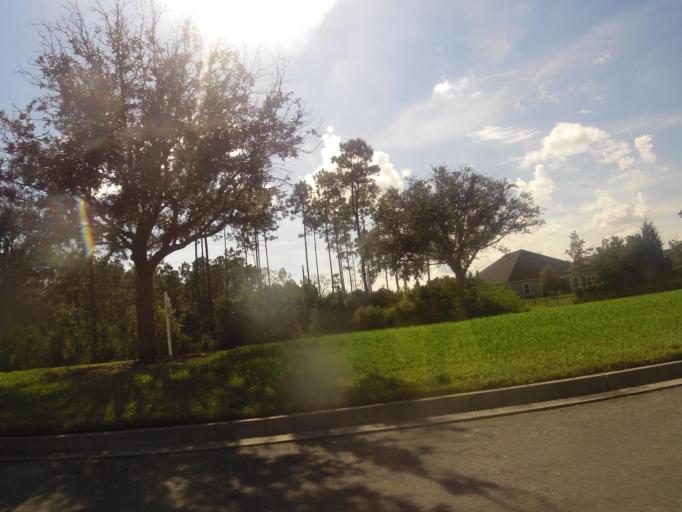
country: US
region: Florida
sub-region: Saint Johns County
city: Palm Valley
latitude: 30.0825
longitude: -81.4711
